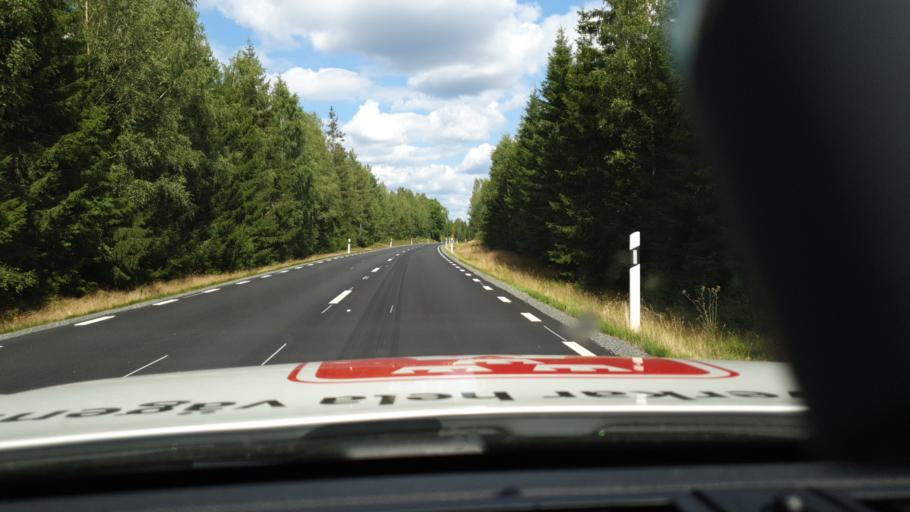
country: SE
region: Joenkoeping
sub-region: Vaggeryds Kommun
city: Skillingaryd
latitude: 57.4075
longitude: 14.0653
